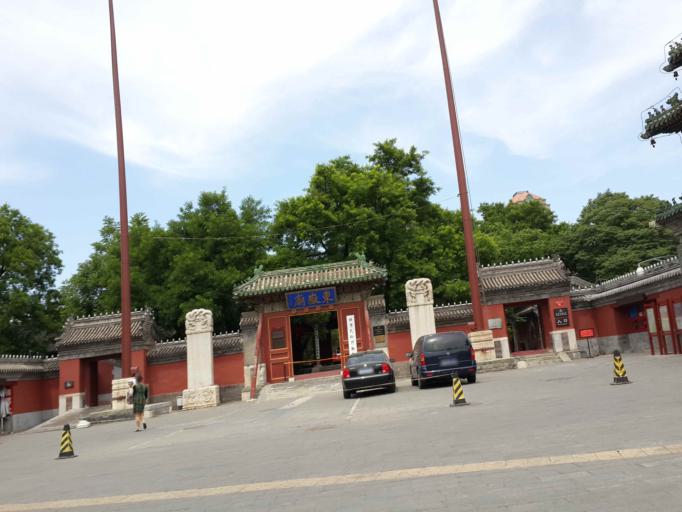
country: CN
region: Beijing
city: Chaowai
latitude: 39.9224
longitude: 116.4377
